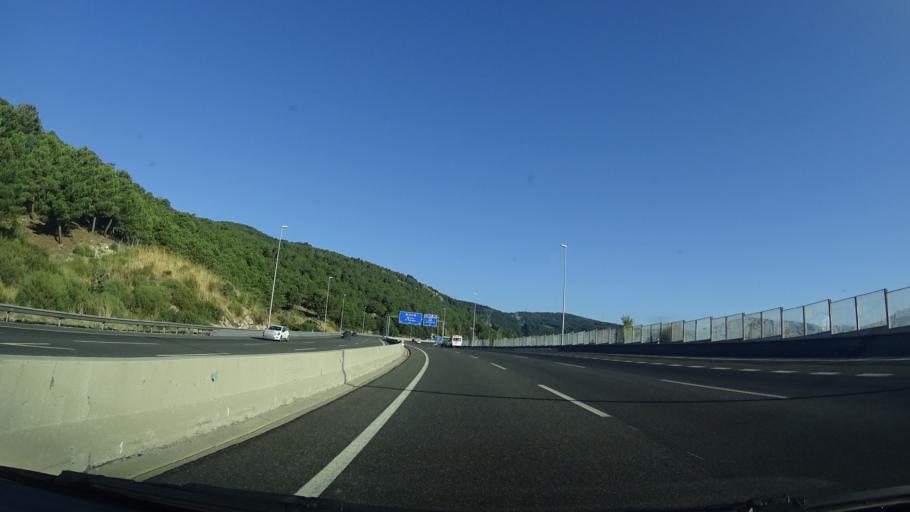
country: ES
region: Madrid
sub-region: Provincia de Madrid
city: Guadarrama
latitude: 40.6864
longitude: -4.1186
